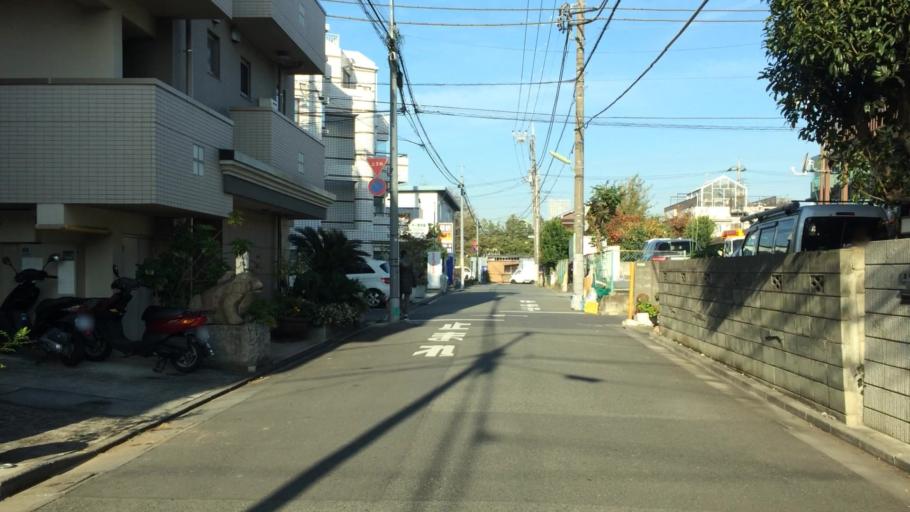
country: JP
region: Tokyo
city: Tokyo
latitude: 35.5983
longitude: 139.6471
